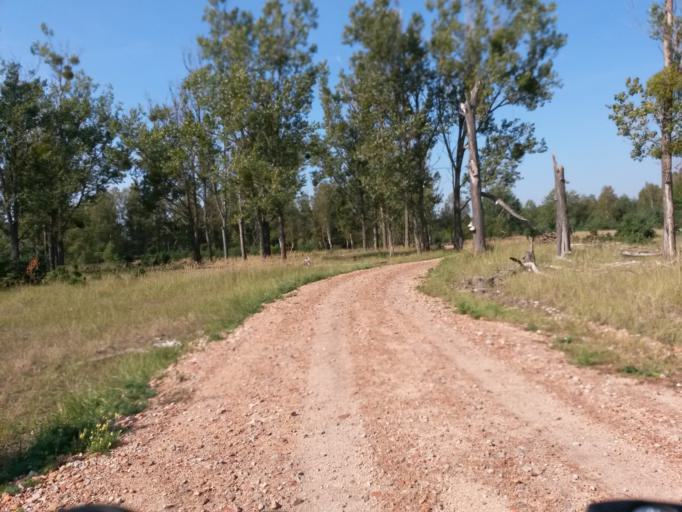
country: DE
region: Brandenburg
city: Zehdenick
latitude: 53.0636
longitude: 13.3722
